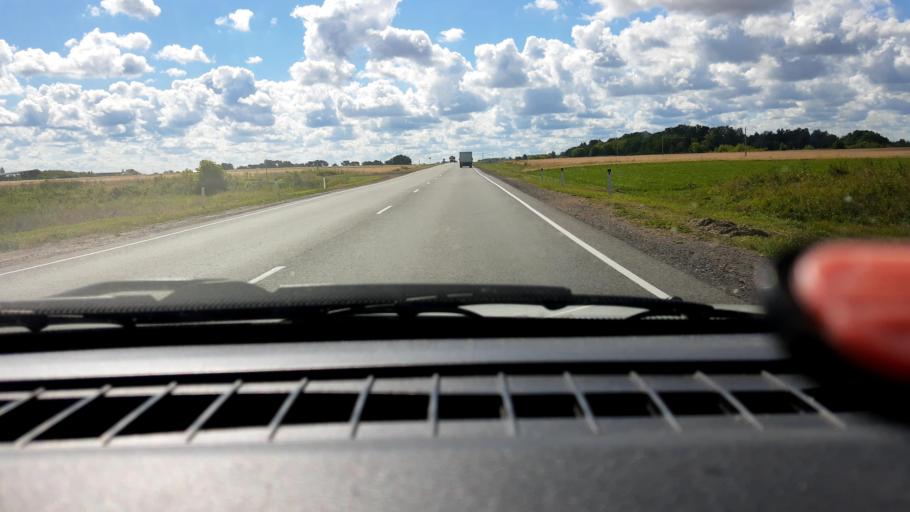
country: RU
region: Nizjnij Novgorod
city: Arzamas
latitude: 55.2729
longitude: 43.9631
